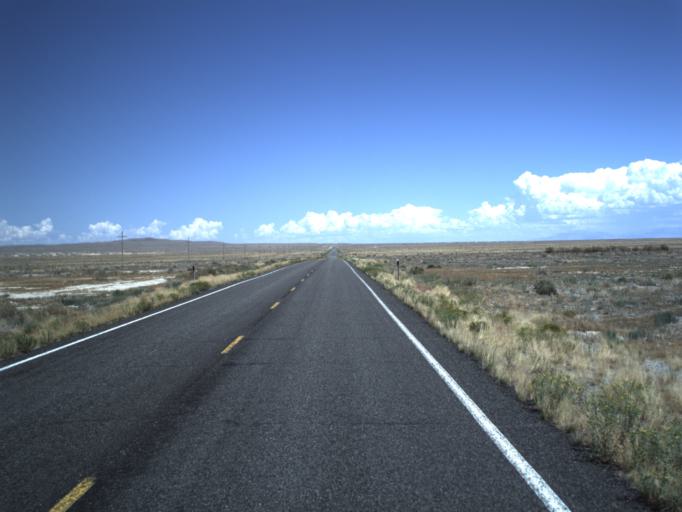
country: US
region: Utah
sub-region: Millard County
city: Delta
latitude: 39.1022
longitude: -113.1514
